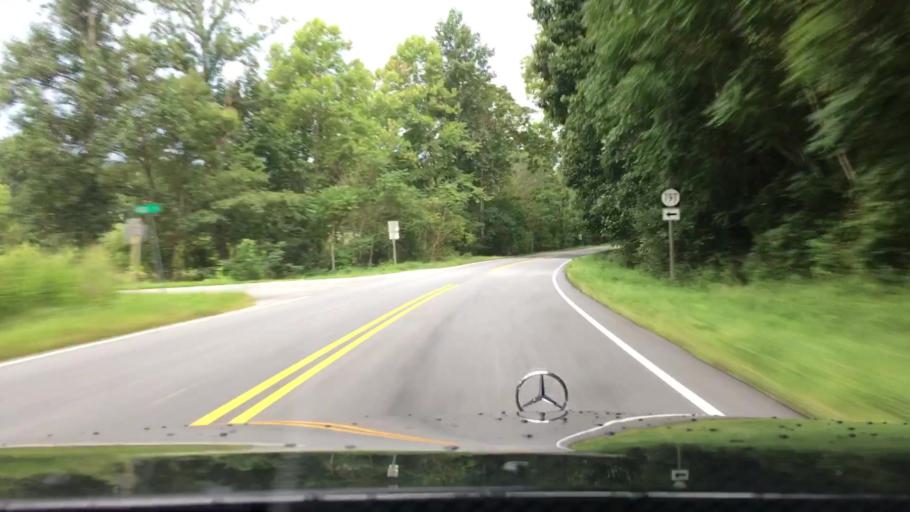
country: US
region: Virginia
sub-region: Nelson County
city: Lovingston
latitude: 37.8172
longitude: -78.9365
